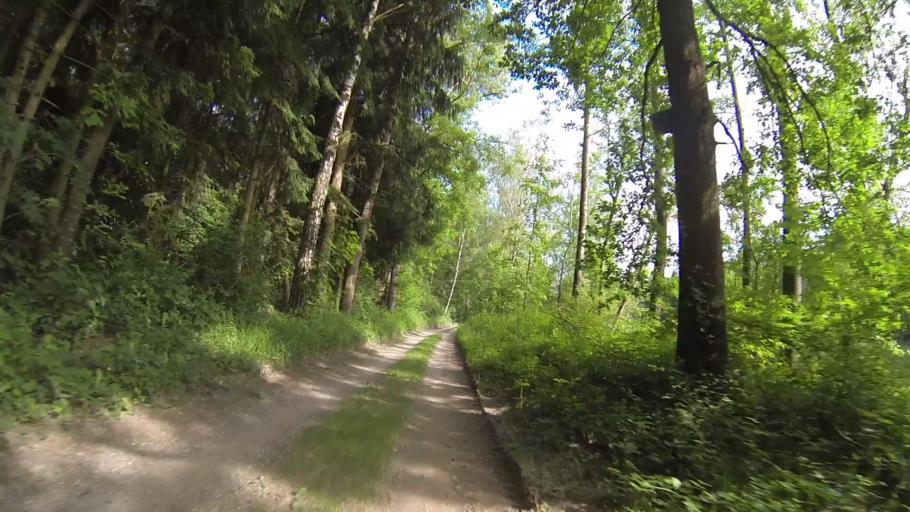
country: DE
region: Bavaria
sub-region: Swabia
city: Senden
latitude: 48.3337
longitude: 10.0155
